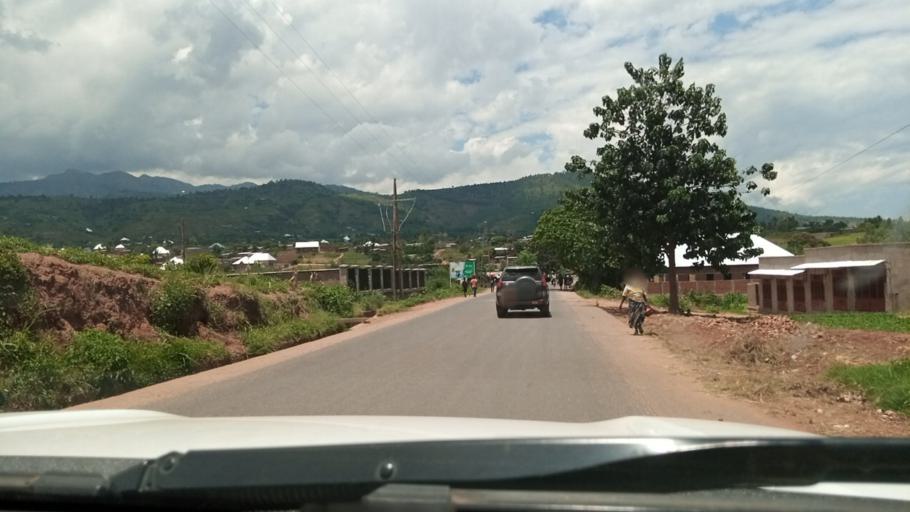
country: BI
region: Bujumbura Mairie
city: Bujumbura
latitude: -3.4782
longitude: 29.3526
